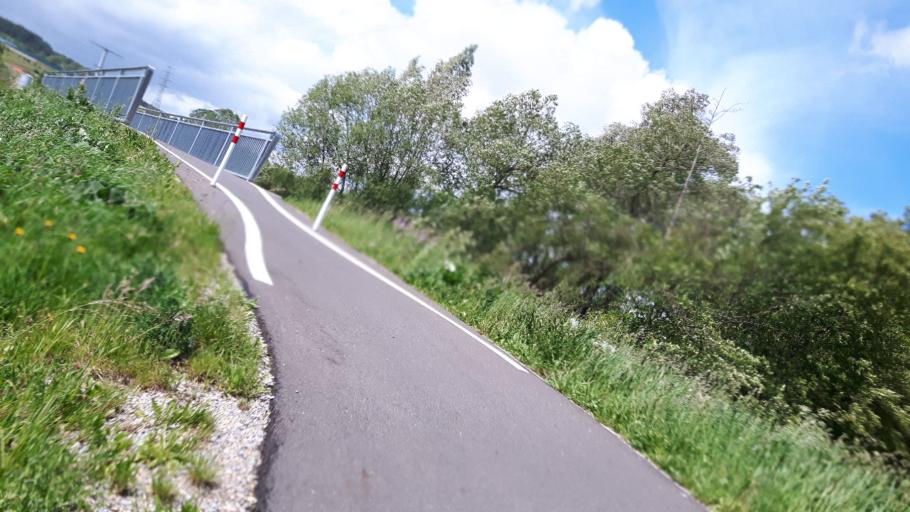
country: DE
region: Thuringia
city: Pennewitz
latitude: 50.6956
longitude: 11.0165
